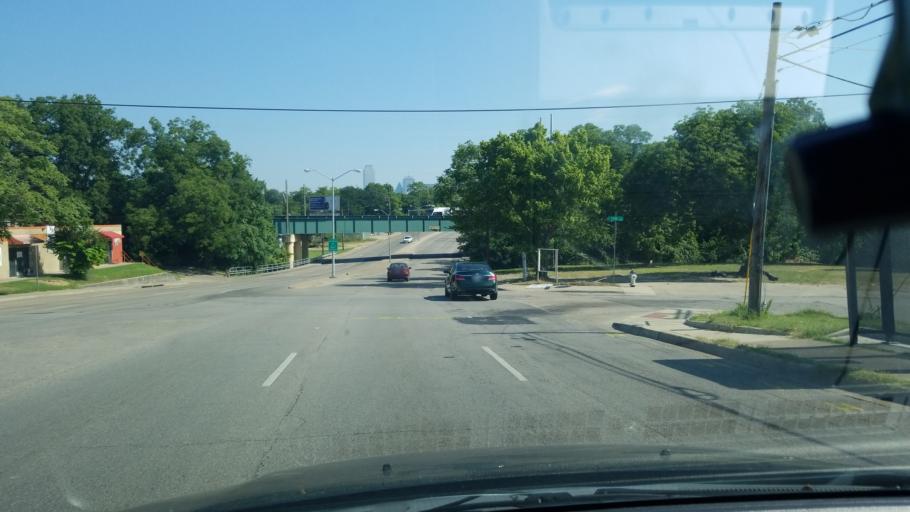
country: US
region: Texas
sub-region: Dallas County
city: Dallas
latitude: 32.7463
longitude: -96.7994
